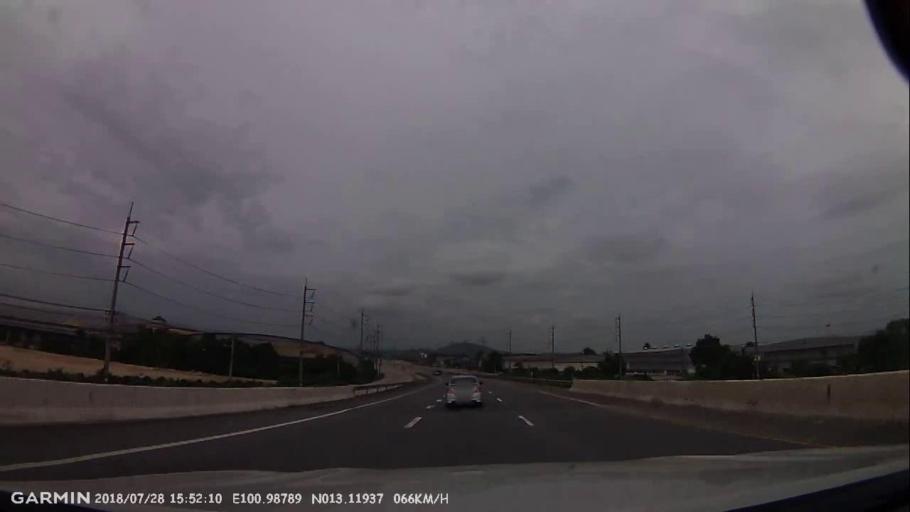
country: TH
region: Chon Buri
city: Ban Talat Bueng
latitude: 13.1193
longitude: 100.9881
